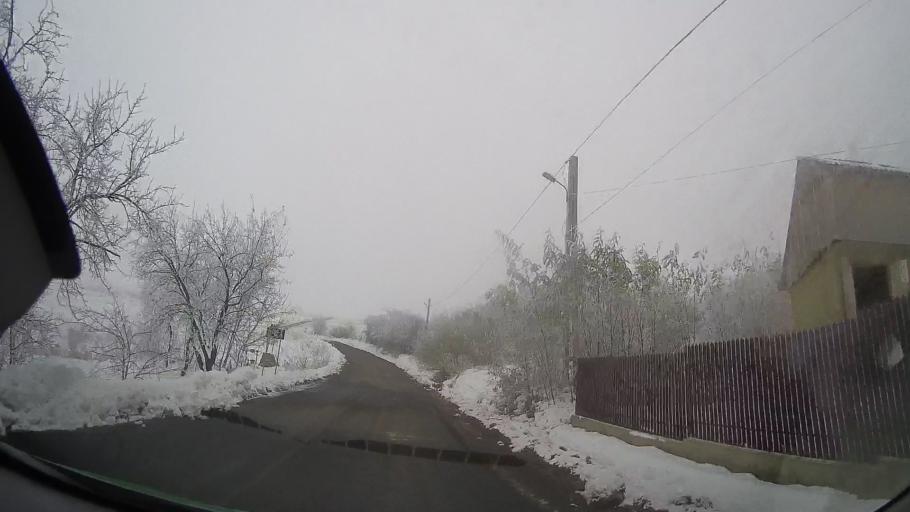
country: RO
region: Iasi
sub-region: Comuna Tansa
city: Suhulet
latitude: 46.8887
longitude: 27.2776
